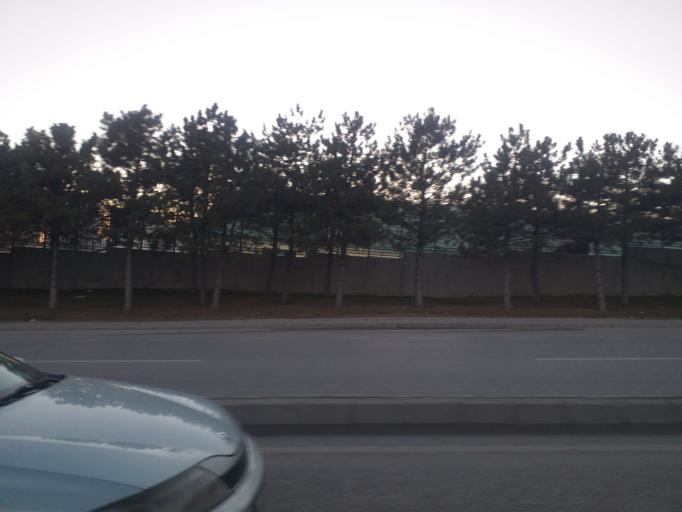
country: TR
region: Ankara
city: Ankara
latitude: 39.9598
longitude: 32.8228
